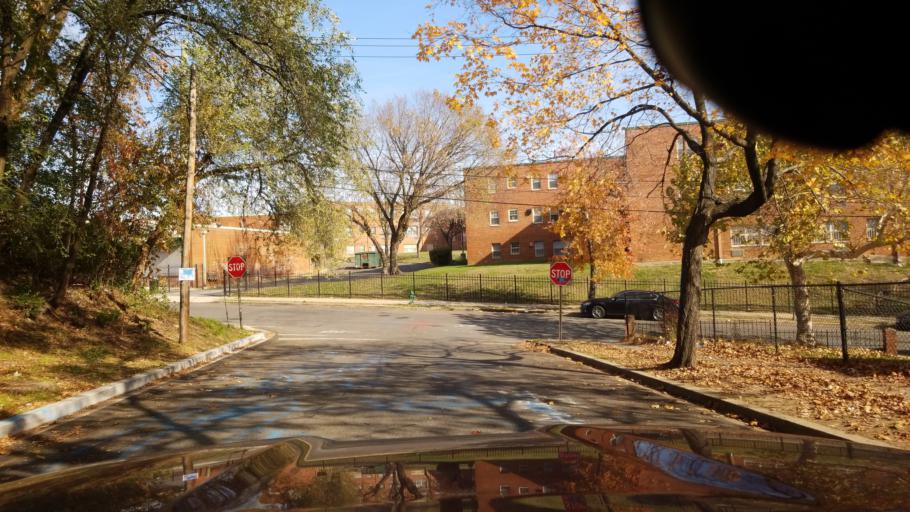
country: US
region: Maryland
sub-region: Prince George's County
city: Hillcrest Heights
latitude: 38.8501
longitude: -76.9746
